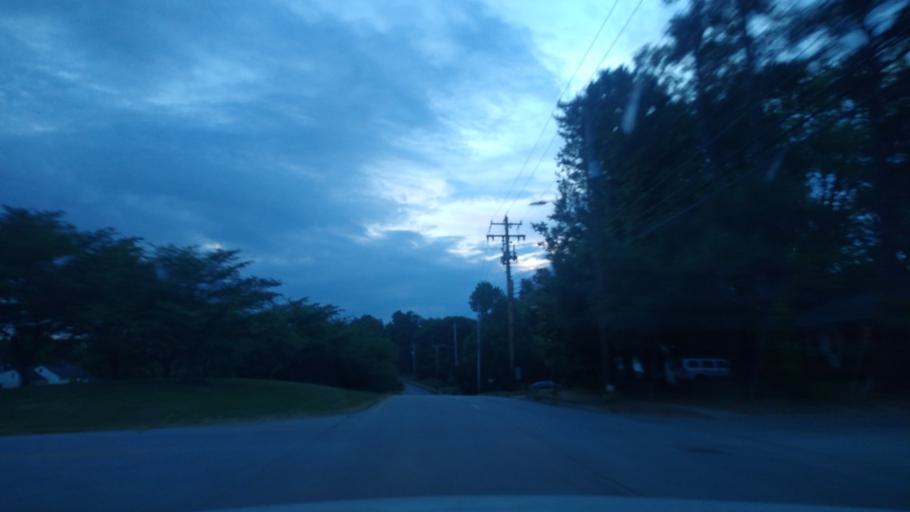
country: US
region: North Carolina
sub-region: Guilford County
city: Greensboro
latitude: 36.1136
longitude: -79.7698
